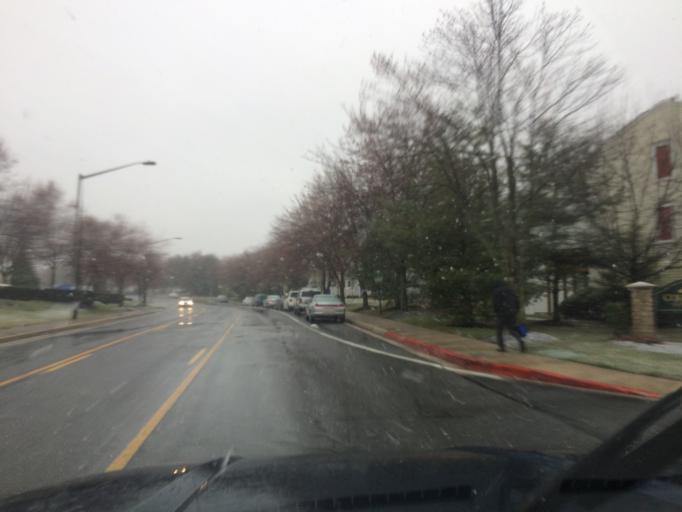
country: US
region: Maryland
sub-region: Howard County
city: Columbia
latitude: 39.2334
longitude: -76.8159
